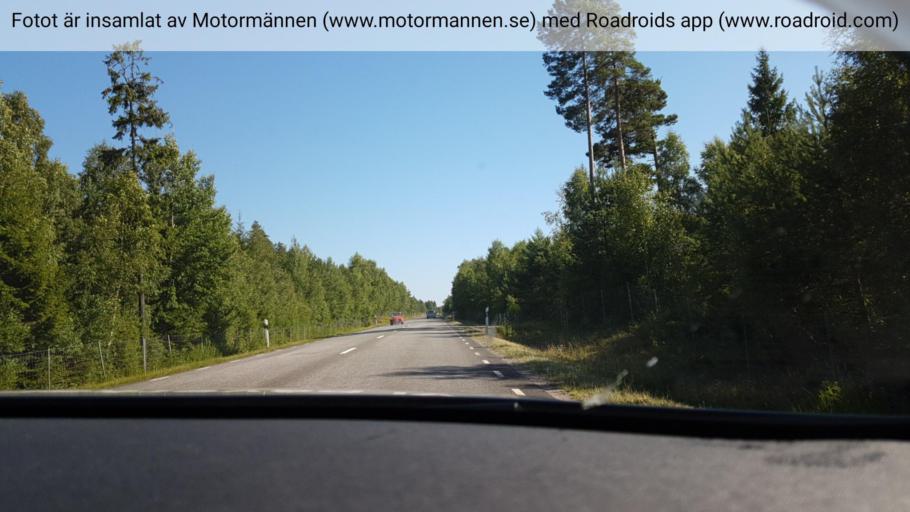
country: SE
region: Vaestra Goetaland
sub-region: Skara Kommun
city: Skara
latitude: 58.3484
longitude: 13.4318
